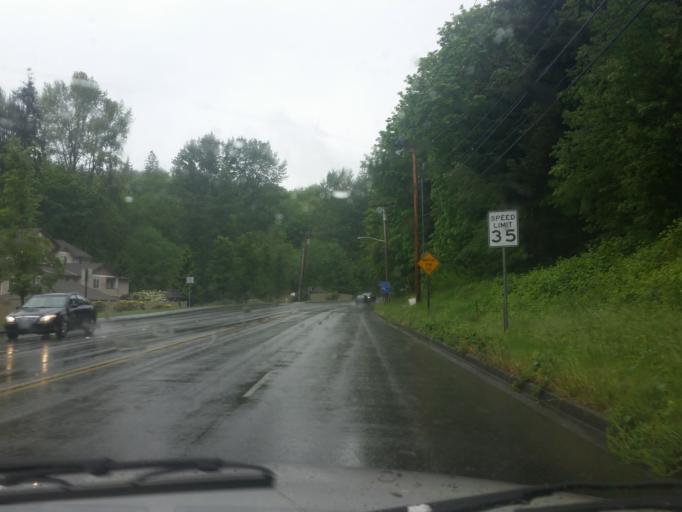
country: US
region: Washington
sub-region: King County
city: Inglewood-Finn Hill
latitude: 47.7309
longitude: -122.2087
